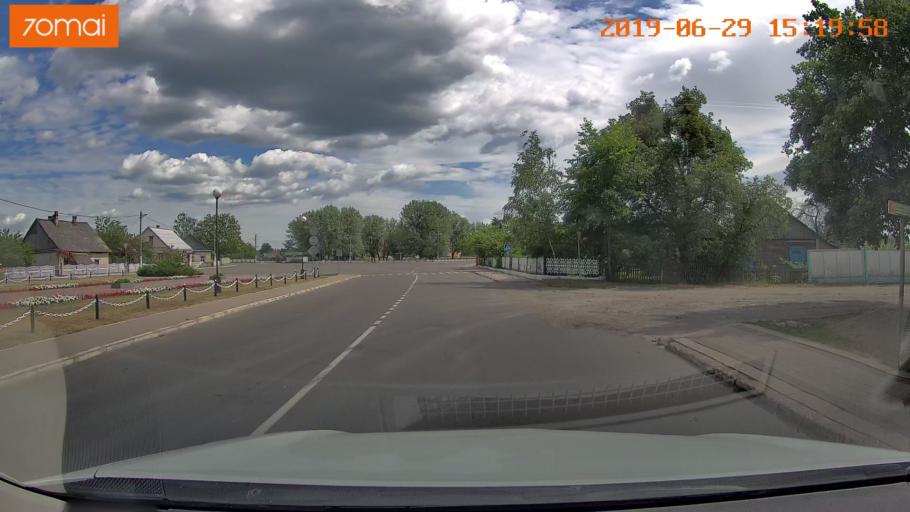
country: BY
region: Brest
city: Mikashevichy
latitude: 52.2169
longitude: 27.4707
